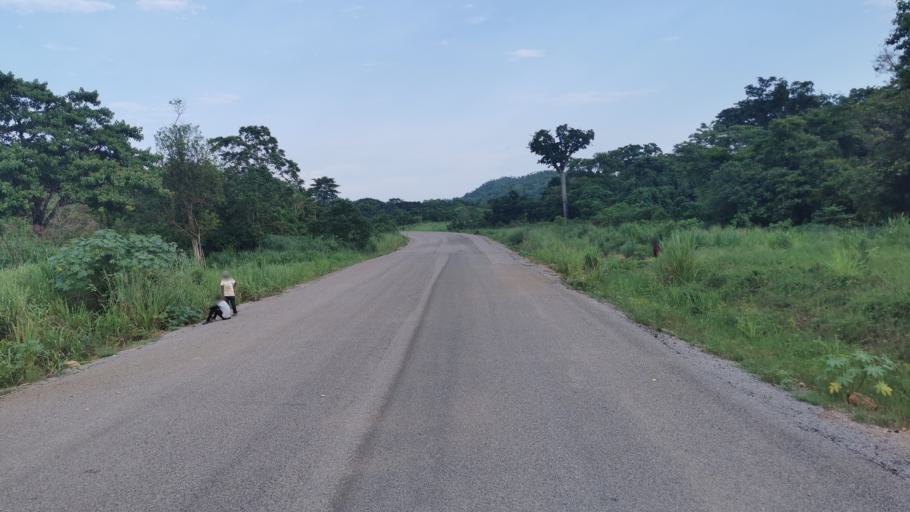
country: ET
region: Gambela
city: Gambela
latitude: 7.6210
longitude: 34.6928
